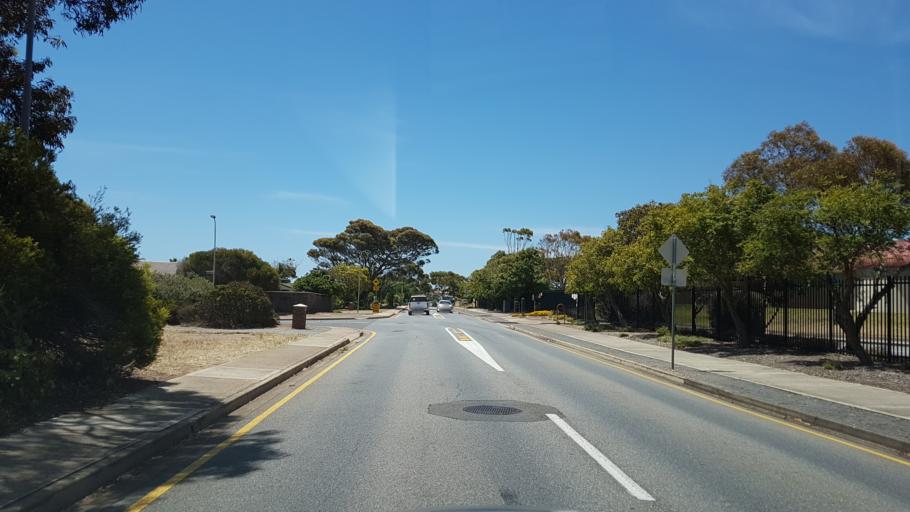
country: AU
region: South Australia
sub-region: Marion
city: Happy Valley
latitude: -35.0762
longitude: 138.5096
